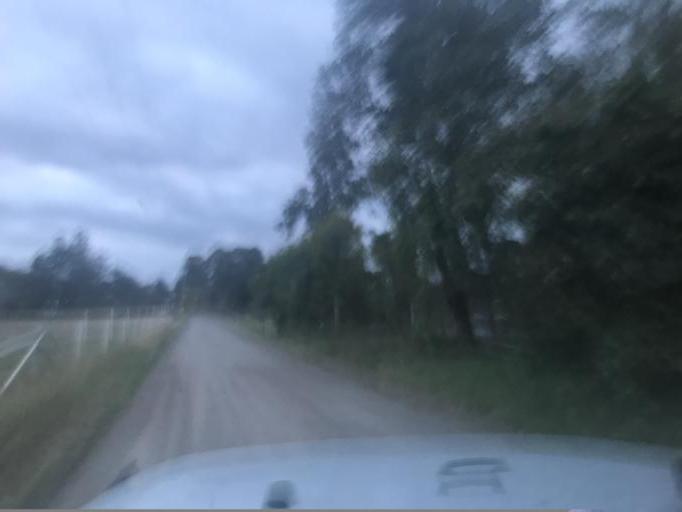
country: AU
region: New South Wales
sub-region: Hawkesbury
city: Pitt Town
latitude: -33.4922
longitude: 150.8862
